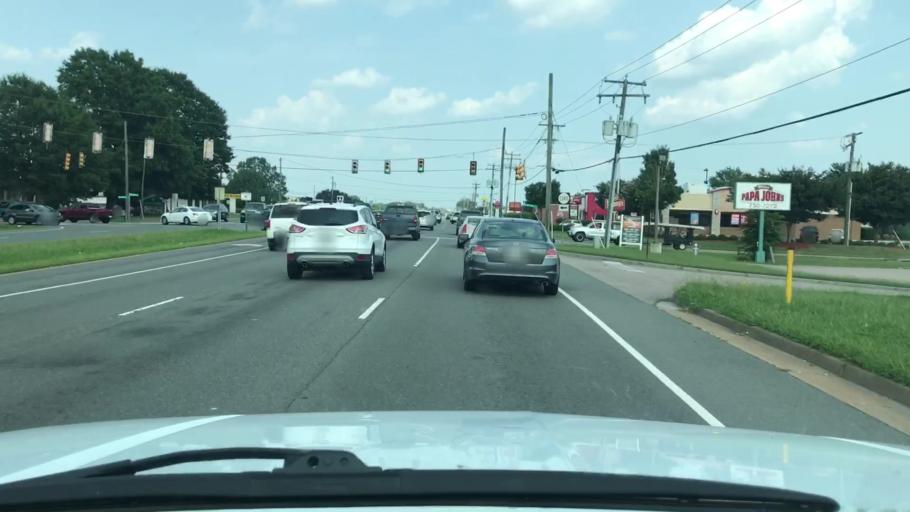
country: US
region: Virginia
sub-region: Hanover County
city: Mechanicsville
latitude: 37.6110
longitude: -77.3440
